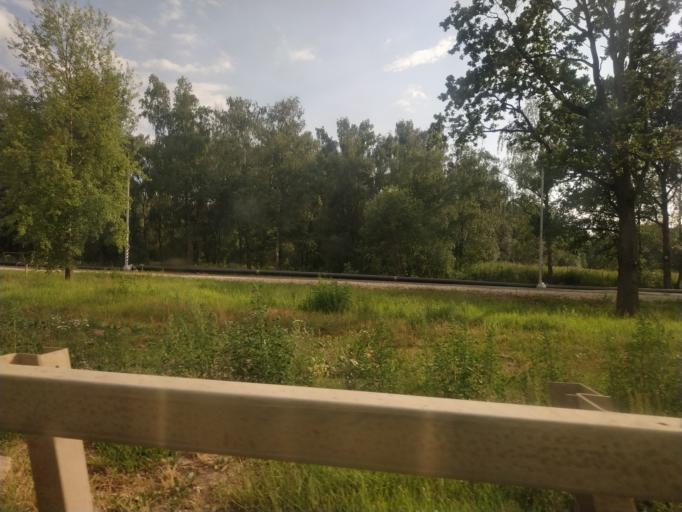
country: RU
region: Moskovskaya
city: Mosrentgen
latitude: 55.5863
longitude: 37.4576
